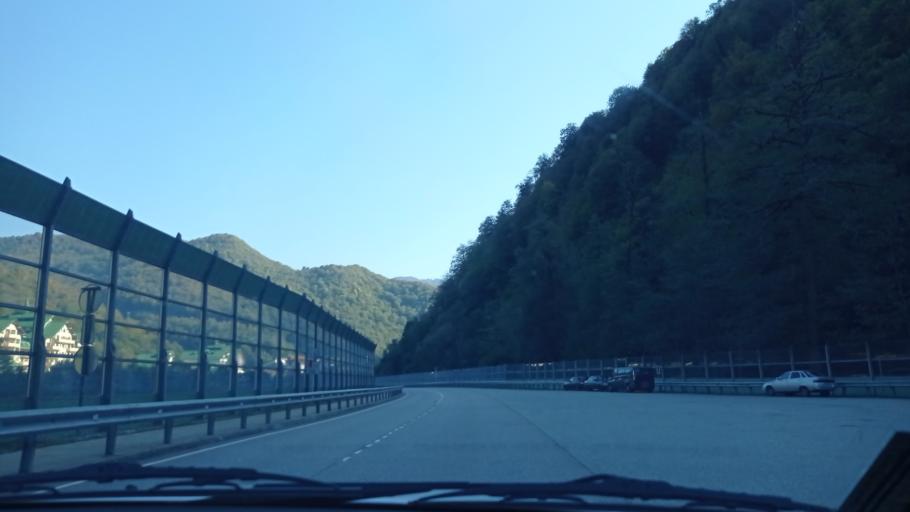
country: RU
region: Krasnodarskiy
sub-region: Sochi City
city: Krasnaya Polyana
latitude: 43.6919
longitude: 40.2709
